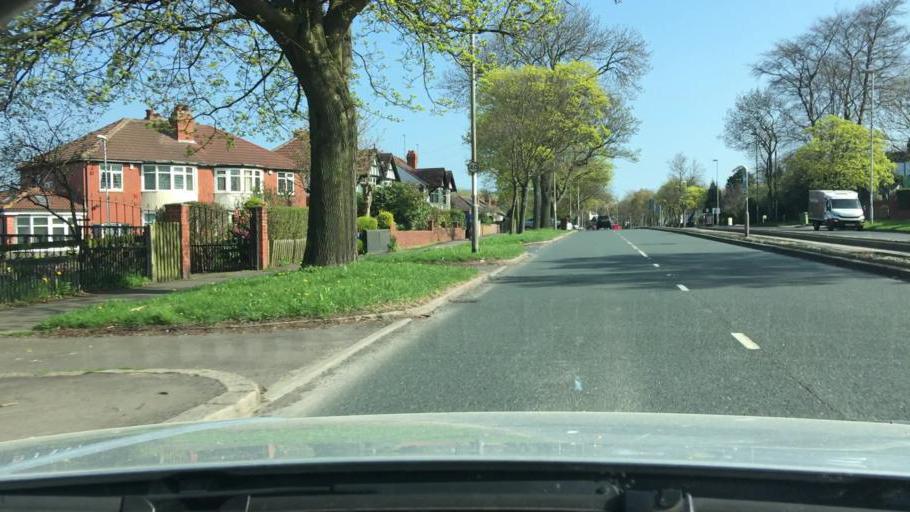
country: GB
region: England
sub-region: City and Borough of Leeds
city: Chapel Allerton
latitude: 53.8309
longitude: -1.5453
